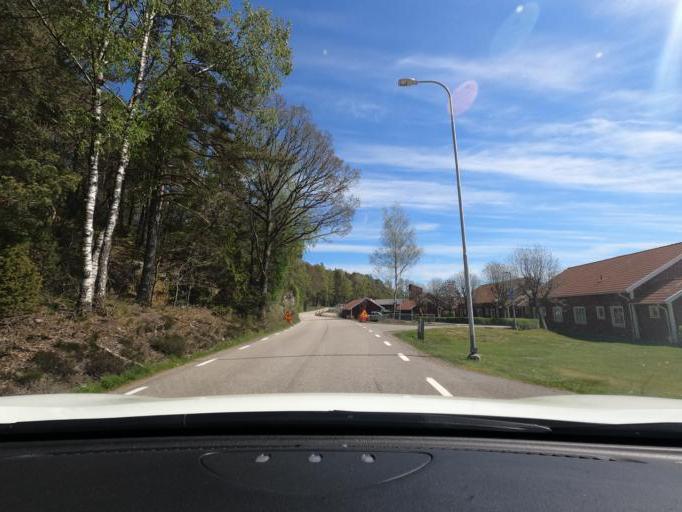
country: SE
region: Vaestra Goetaland
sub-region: Marks Kommun
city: Horred
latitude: 57.4245
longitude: 12.3332
